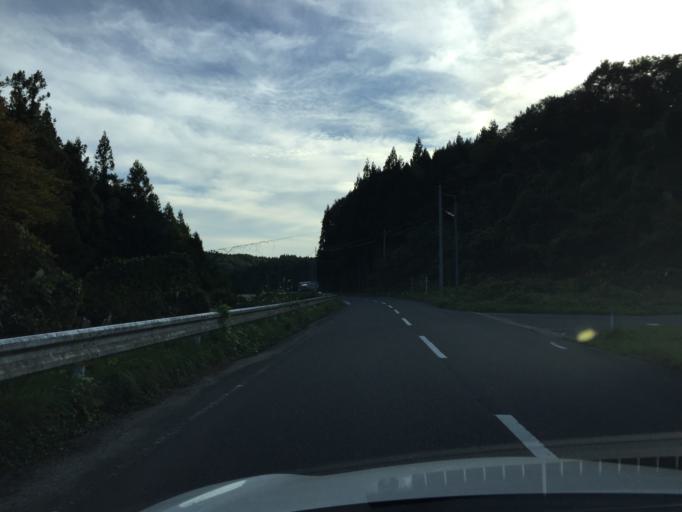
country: JP
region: Fukushima
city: Ishikawa
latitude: 37.2049
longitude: 140.5480
